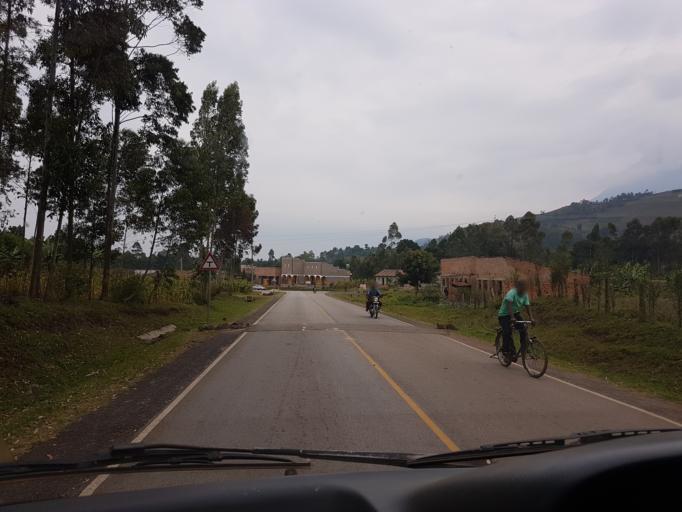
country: UG
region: Western Region
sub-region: Kisoro District
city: Kisoro
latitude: -1.3118
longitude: 29.7210
